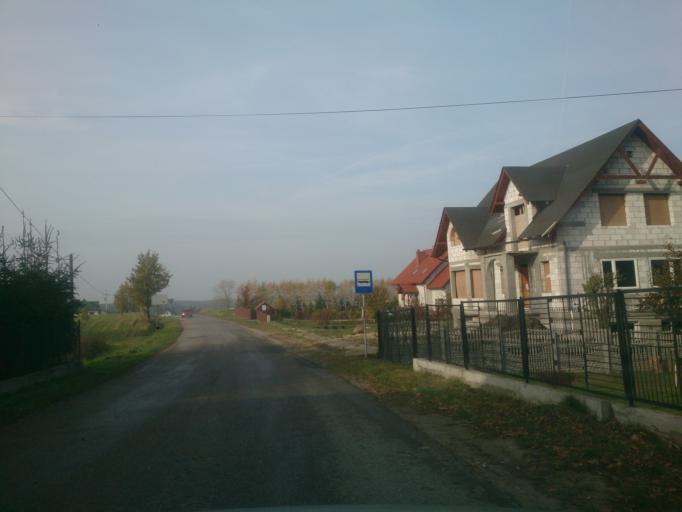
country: PL
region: Kujawsko-Pomorskie
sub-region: Powiat brodnicki
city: Brodnica
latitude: 53.3337
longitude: 19.3752
